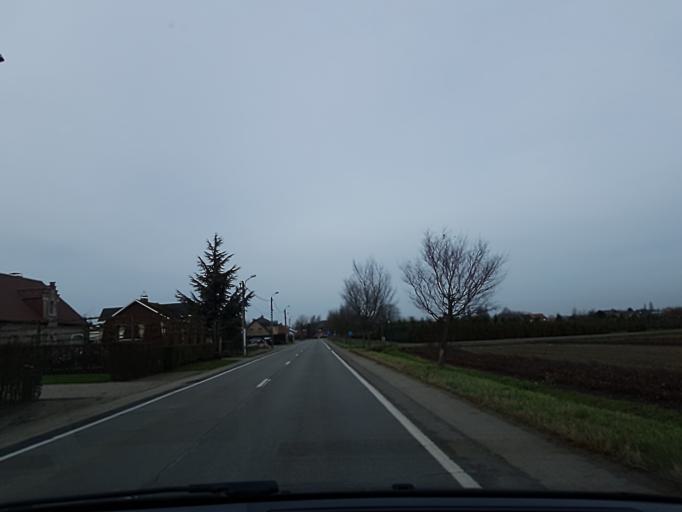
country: BE
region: Flanders
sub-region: Provincie Antwerpen
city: Putte
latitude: 51.0647
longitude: 4.6280
